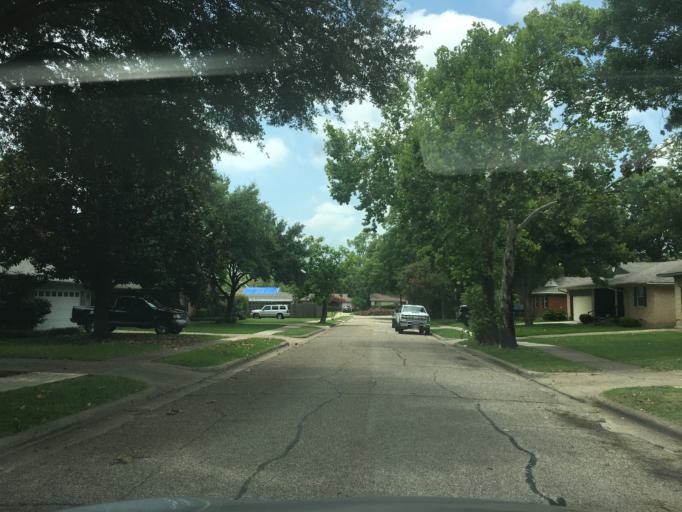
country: US
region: Texas
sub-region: Dallas County
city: Richardson
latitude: 32.9494
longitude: -96.7622
